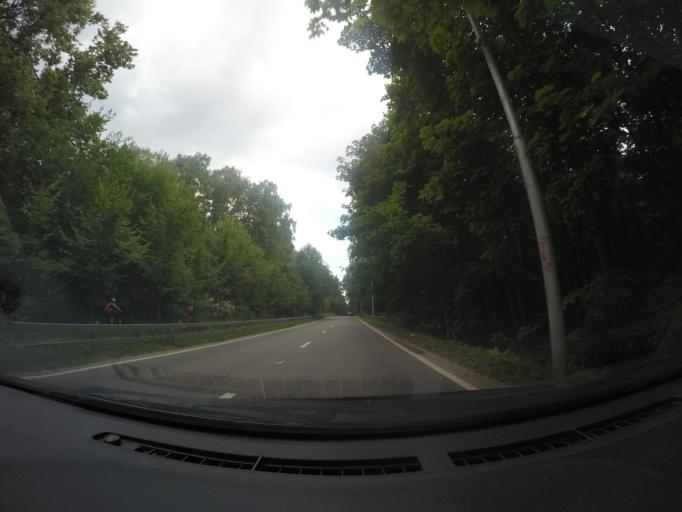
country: RU
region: Moscow
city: Sokol'niki
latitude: 55.8137
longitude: 37.6739
